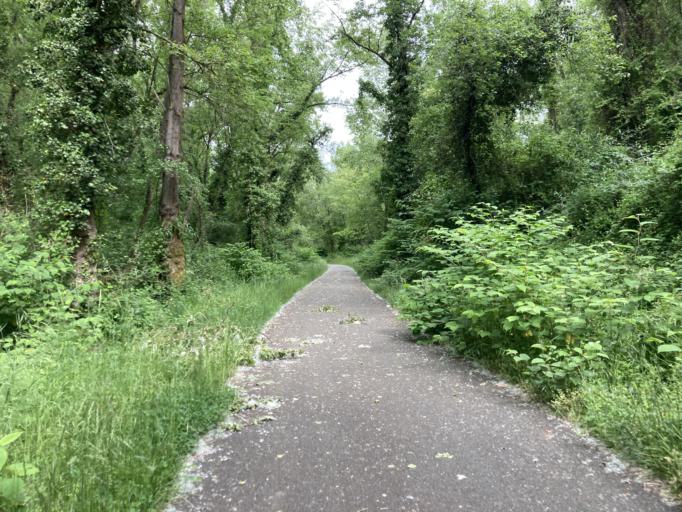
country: FR
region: Aquitaine
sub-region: Departement des Pyrenees-Atlantiques
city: Arbus
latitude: 43.3324
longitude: -0.4867
